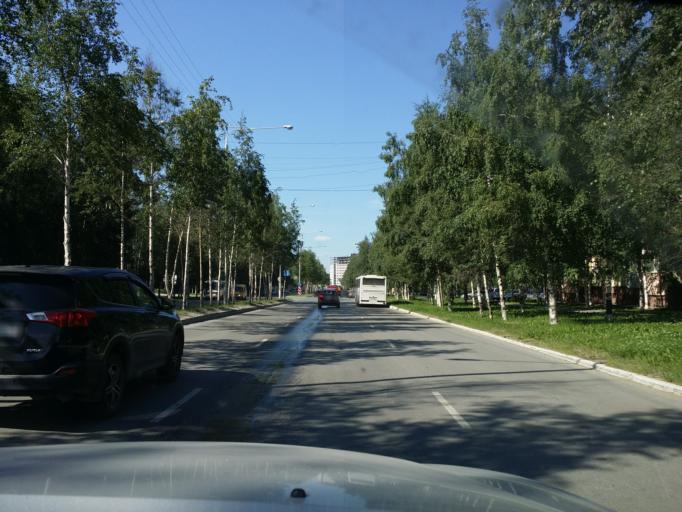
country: RU
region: Khanty-Mansiyskiy Avtonomnyy Okrug
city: Nizhnevartovsk
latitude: 60.9409
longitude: 76.5669
